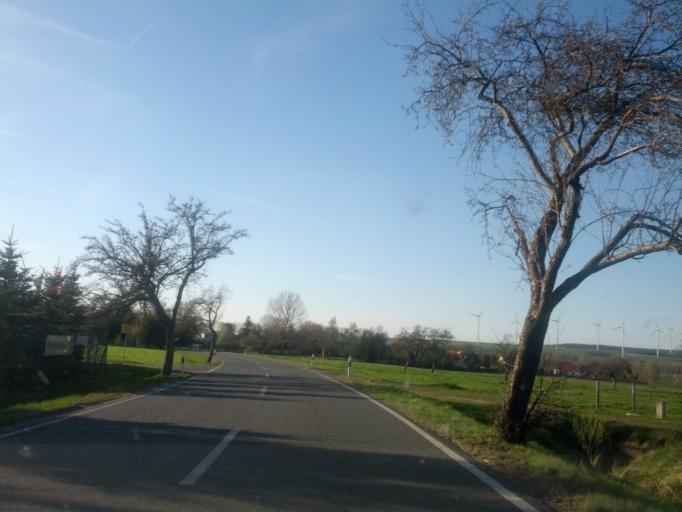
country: DE
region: Thuringia
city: Waltershausen
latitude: 50.9258
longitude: 10.5483
